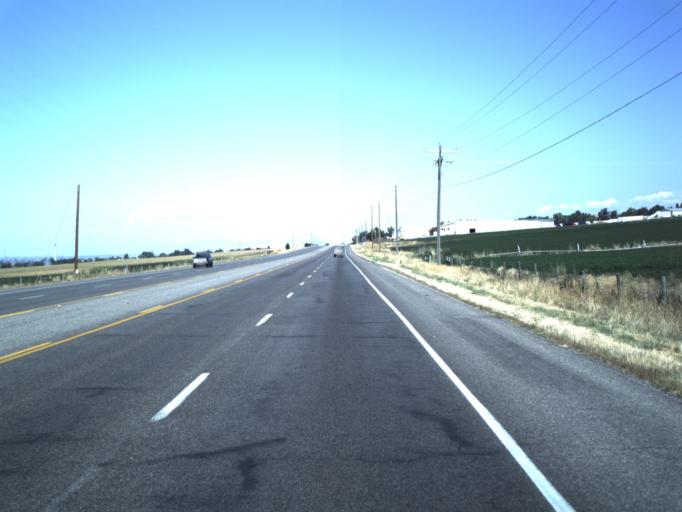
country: US
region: Utah
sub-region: Cache County
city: Richmond
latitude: 41.9002
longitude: -111.8147
